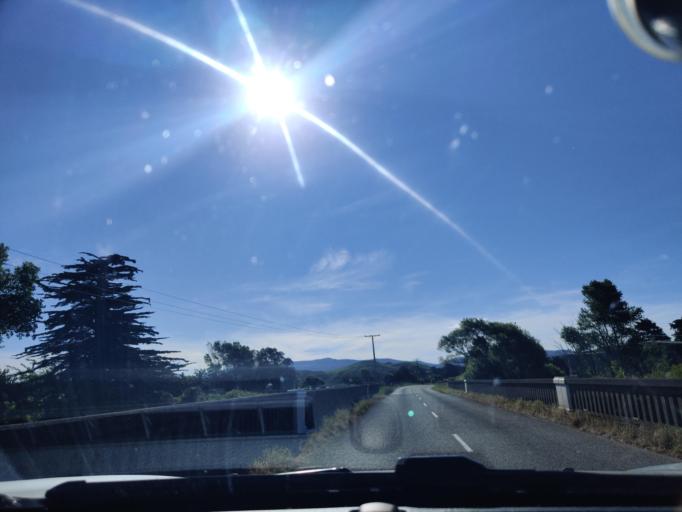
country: NZ
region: Manawatu-Wanganui
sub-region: Palmerston North City
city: Palmerston North
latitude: -40.5202
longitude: 175.7599
